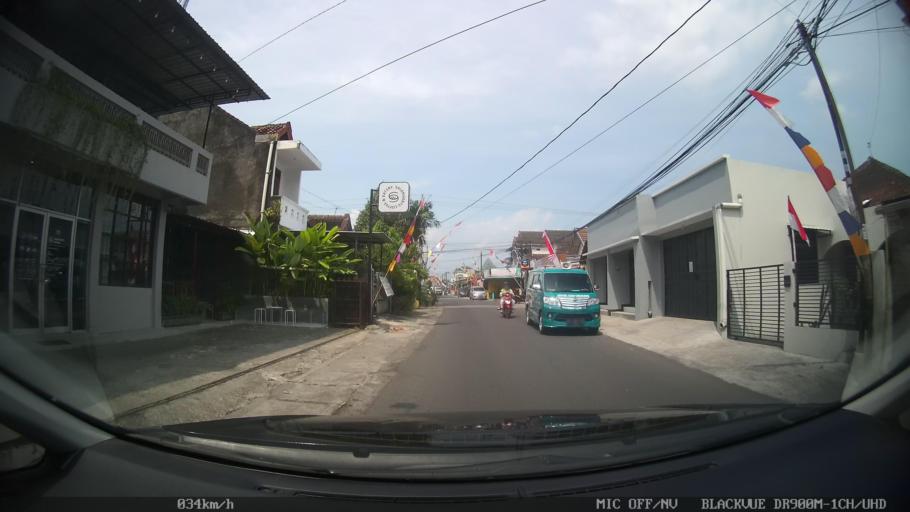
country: ID
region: Daerah Istimewa Yogyakarta
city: Yogyakarta
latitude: -7.7963
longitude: 110.4004
